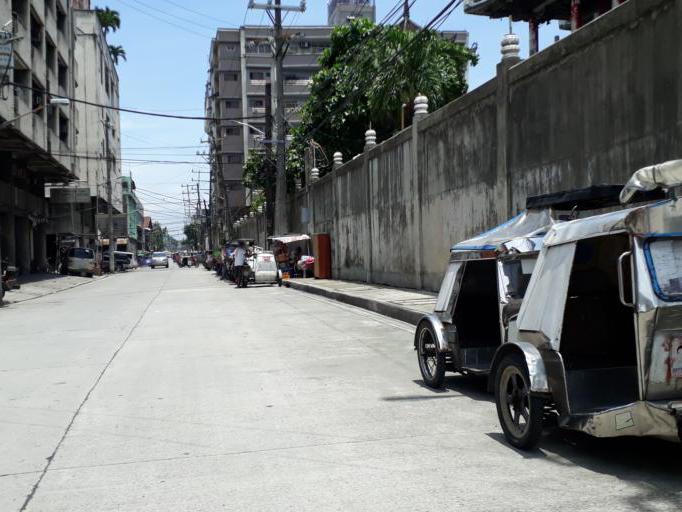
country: PH
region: Calabarzon
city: Del Monte
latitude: 14.6452
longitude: 120.9844
